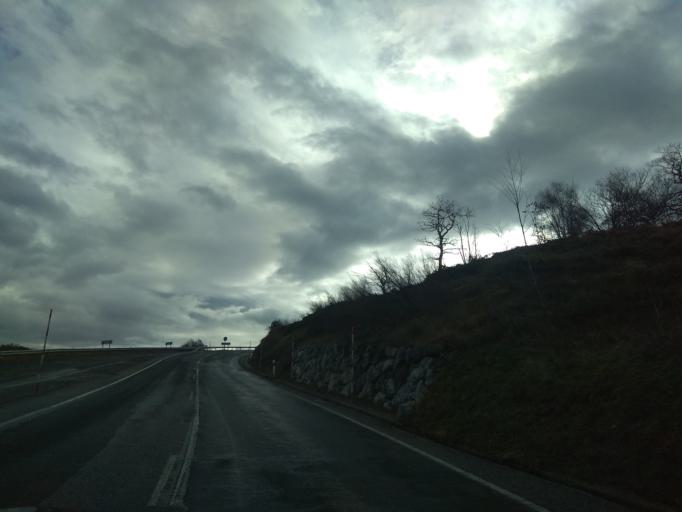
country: ES
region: Castille and Leon
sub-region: Provincia de Burgos
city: Arija
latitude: 43.0596
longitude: -3.8873
